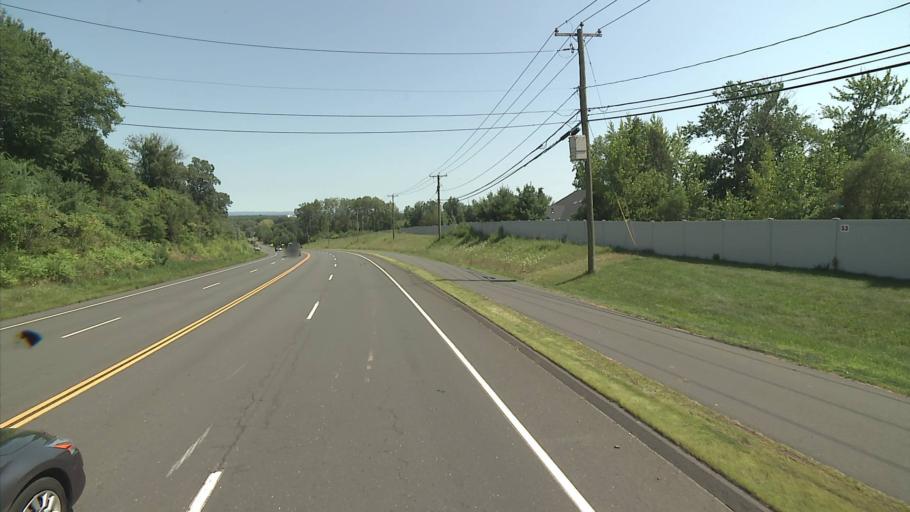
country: US
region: Connecticut
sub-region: Hartford County
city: Tariffville
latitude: 41.9452
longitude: -72.7366
